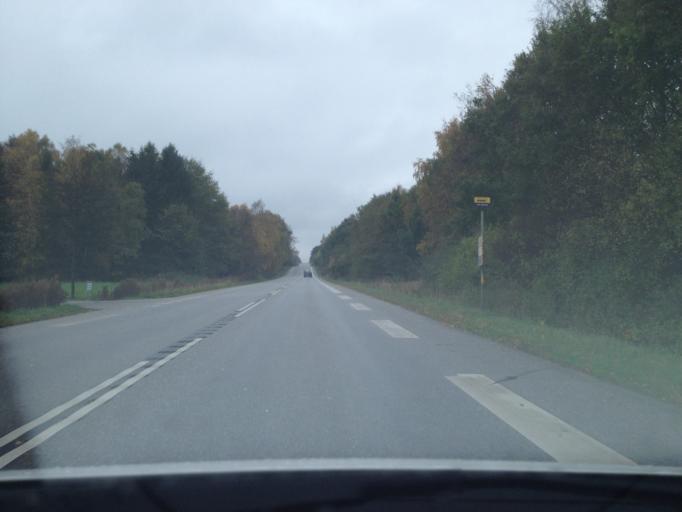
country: DK
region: Capital Region
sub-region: Fredensborg Kommune
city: Fredensborg
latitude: 55.9543
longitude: 12.4166
